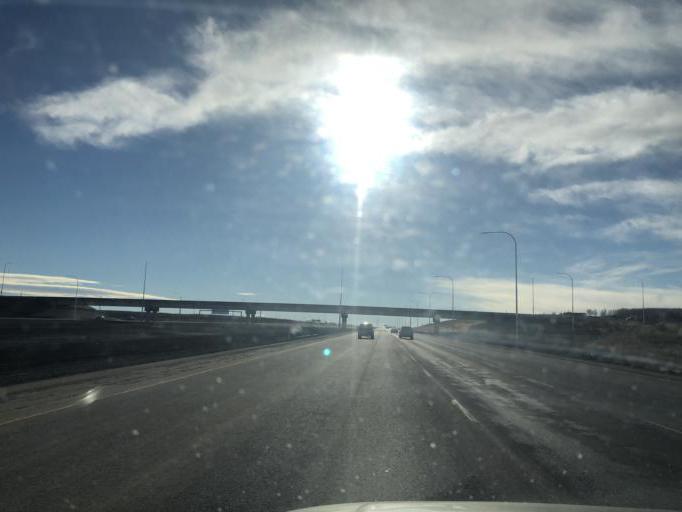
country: CA
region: Alberta
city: Calgary
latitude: 50.9777
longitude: -114.1593
